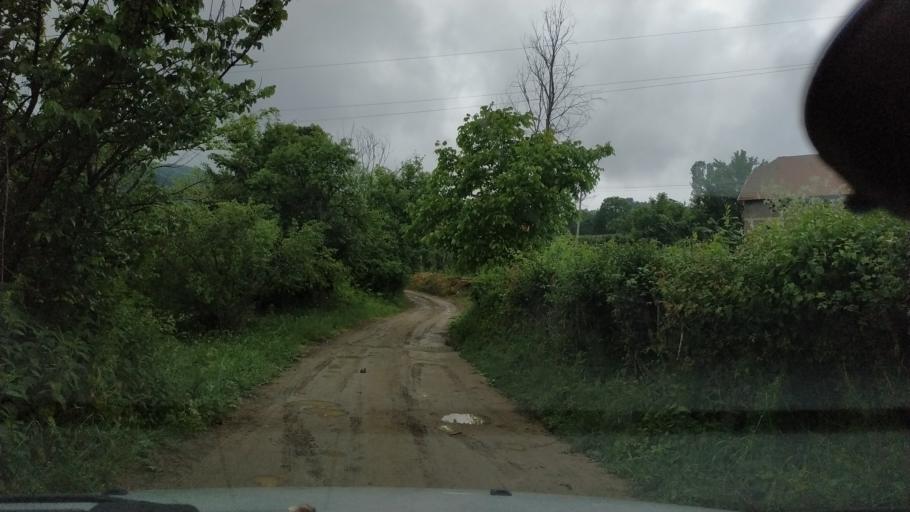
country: RS
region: Central Serbia
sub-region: Toplicki Okrug
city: Prokuplje
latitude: 43.4002
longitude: 21.5579
